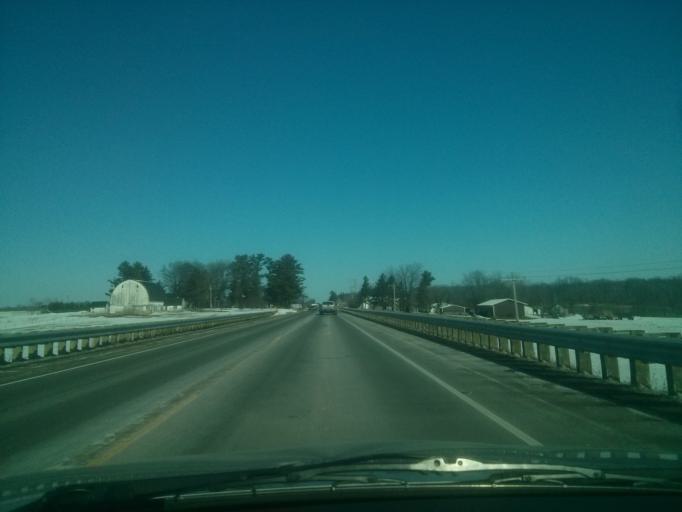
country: US
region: Wisconsin
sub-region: Polk County
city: Clear Lake
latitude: 45.1847
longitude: -92.2833
